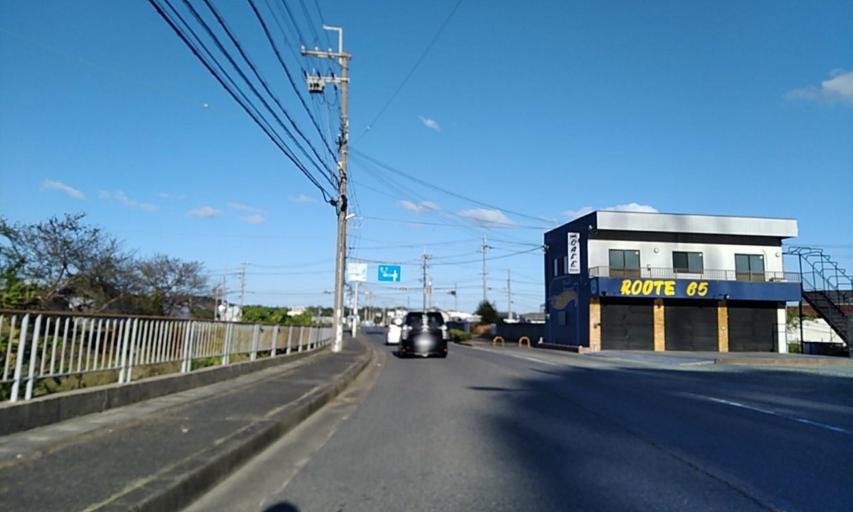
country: JP
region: Wakayama
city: Wakayama-shi
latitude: 34.3172
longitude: 135.1248
